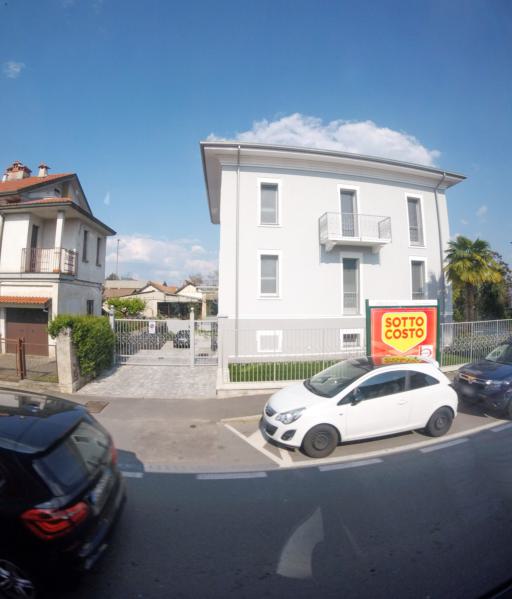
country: IT
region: Piedmont
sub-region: Provincia di Novara
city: Arona
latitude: 45.7511
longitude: 8.5608
